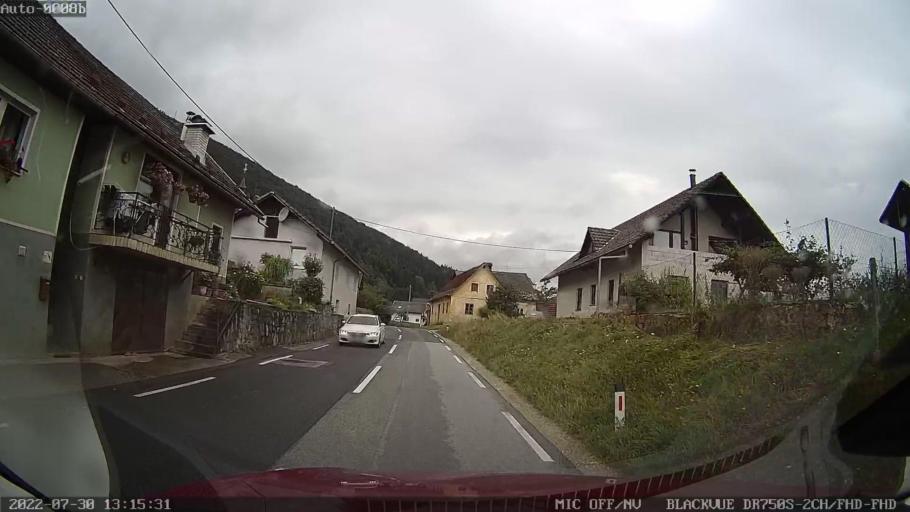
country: SI
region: Dolenjske Toplice
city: Dolenjske Toplice
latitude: 45.7401
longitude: 15.0423
